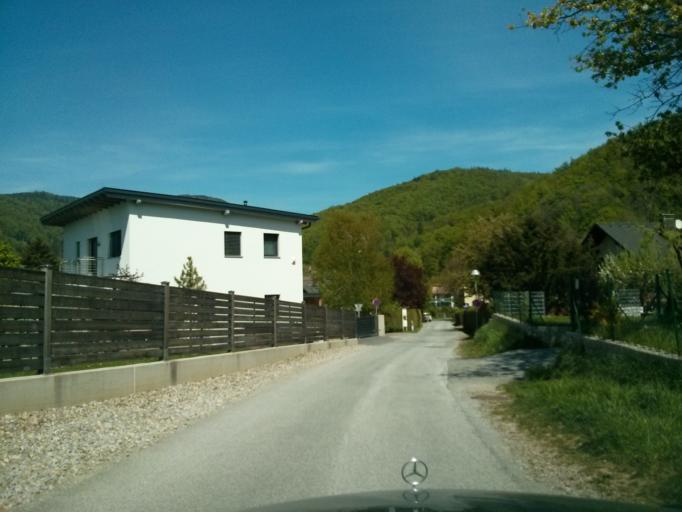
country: AT
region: Styria
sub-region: Politischer Bezirk Graz-Umgebung
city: Stattegg
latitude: 47.1371
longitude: 15.4225
